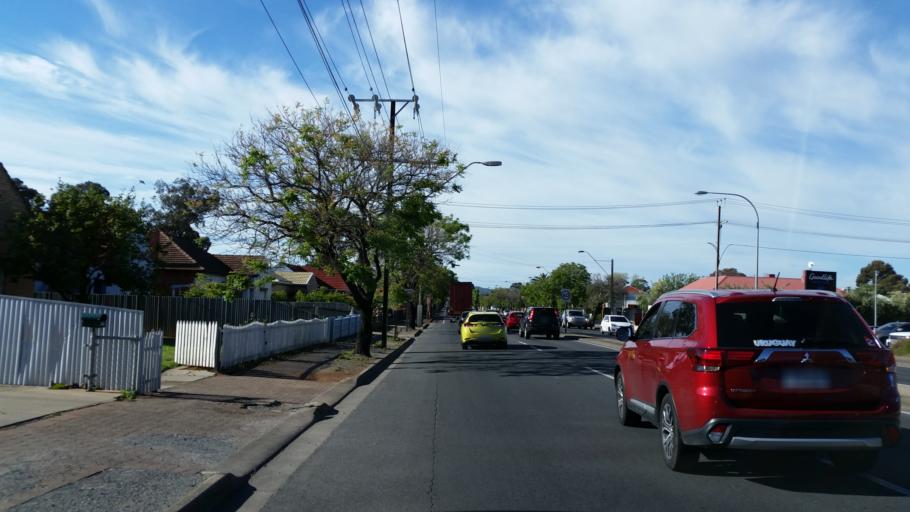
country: AU
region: South Australia
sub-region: Norwood Payneham St Peters
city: Payneham
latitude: -34.8976
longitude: 138.6394
